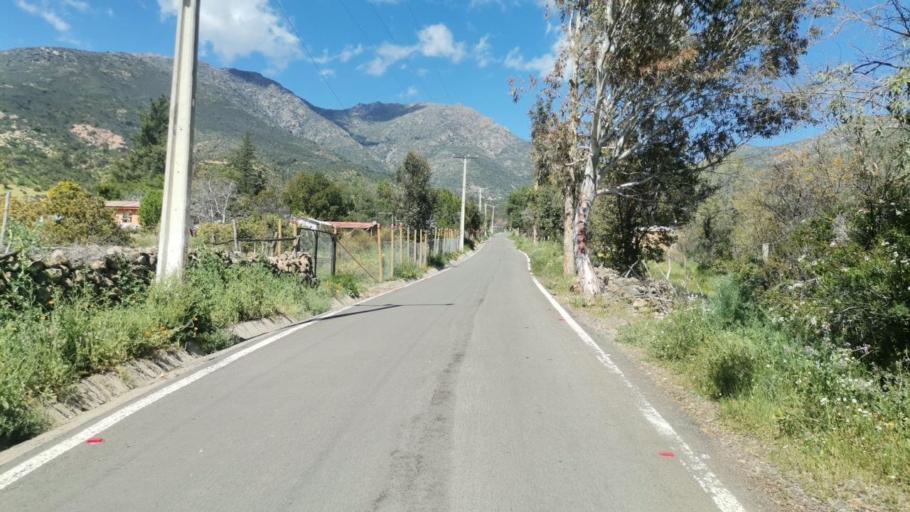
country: CL
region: Valparaiso
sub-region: Provincia de Marga Marga
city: Limache
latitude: -33.1903
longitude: -71.0986
